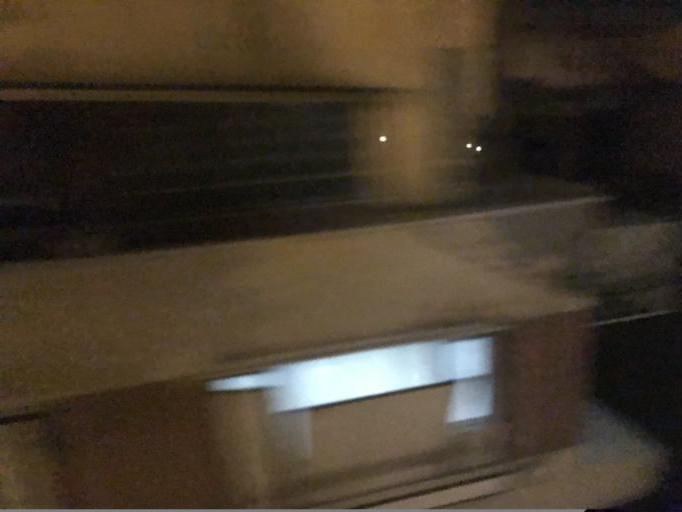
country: TR
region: Istanbul
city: Maltepe
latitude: 40.9261
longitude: 29.1458
